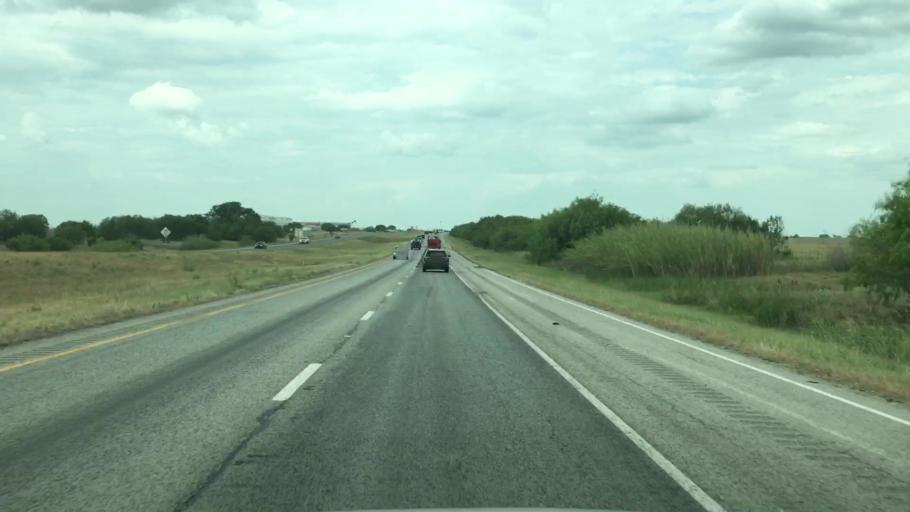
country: US
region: Texas
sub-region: Atascosa County
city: Pleasanton
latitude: 29.0889
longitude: -98.4328
